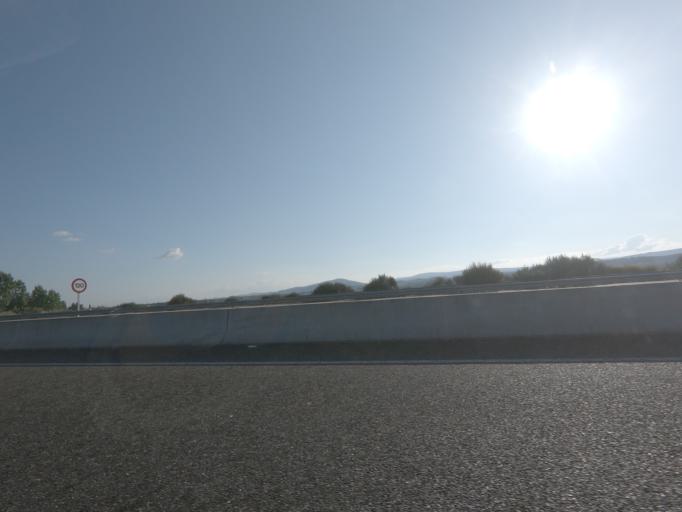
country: ES
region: Galicia
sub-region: Provincia de Ourense
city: Oimbra
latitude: 41.8287
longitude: -7.4211
